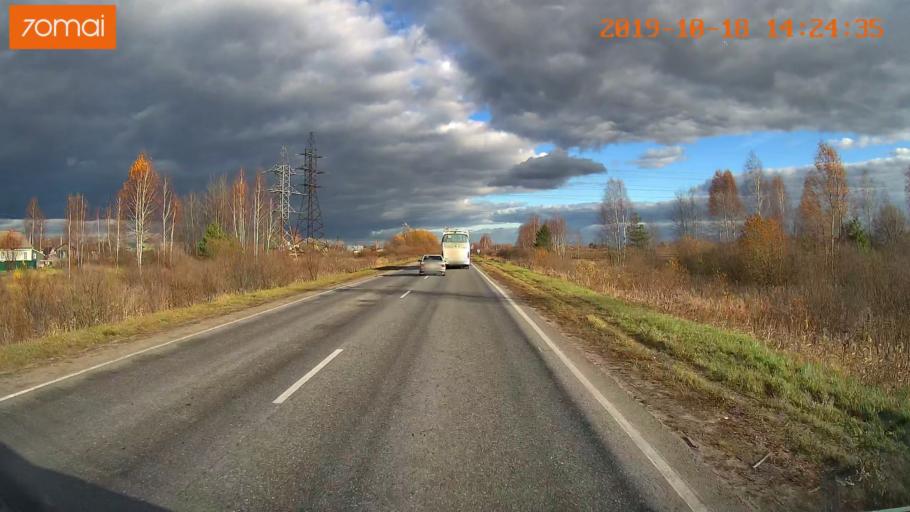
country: RU
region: Rjazan
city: Tuma
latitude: 55.1469
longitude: 40.5022
